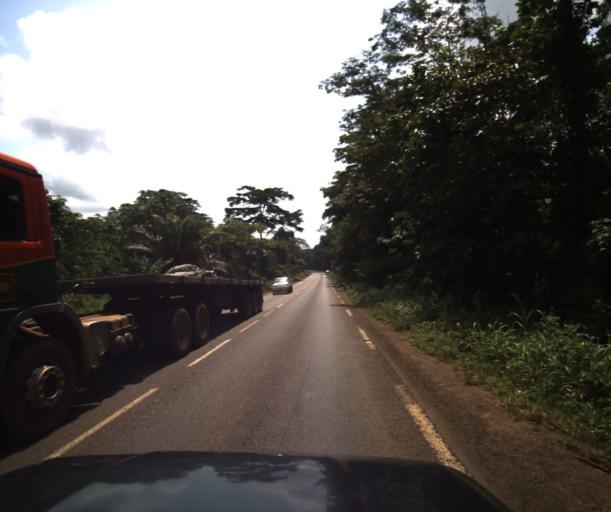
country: CM
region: Centre
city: Eseka
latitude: 3.8911
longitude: 10.7820
